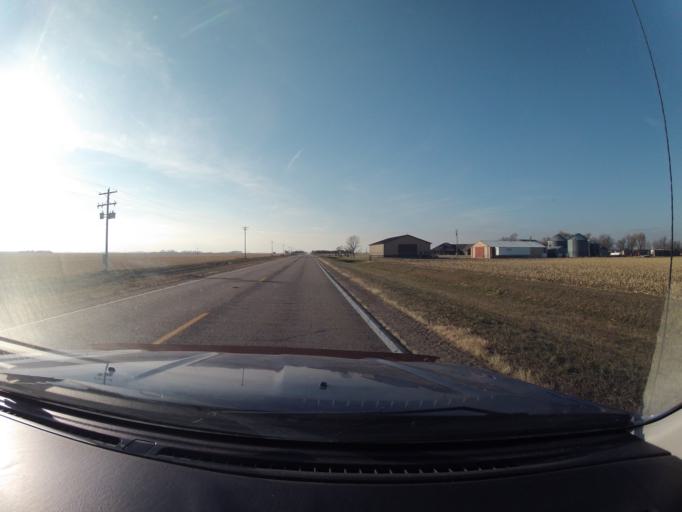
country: US
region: Nebraska
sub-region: Buffalo County
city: Kearney
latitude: 40.6410
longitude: -99.0127
